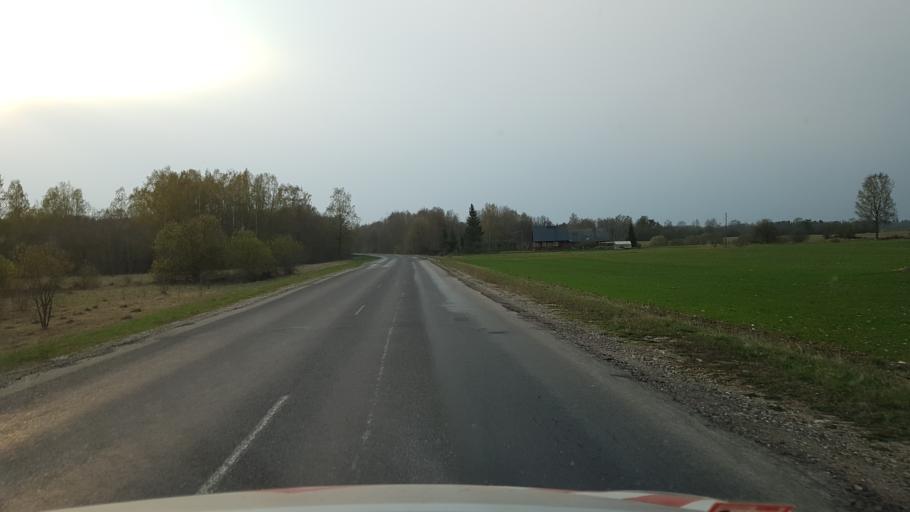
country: EE
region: Harju
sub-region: Raasiku vald
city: Raasiku
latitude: 59.3417
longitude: 25.1359
